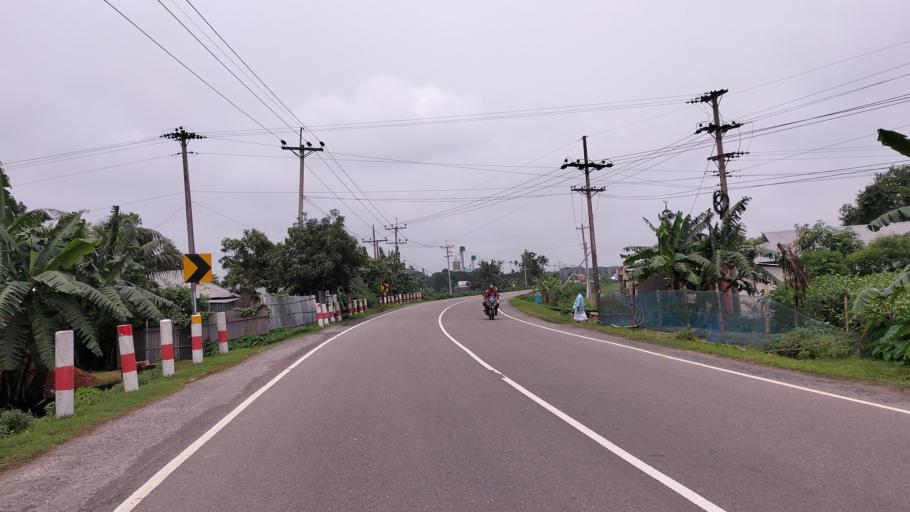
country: BD
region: Dhaka
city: Netrakona
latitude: 24.8526
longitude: 90.6503
